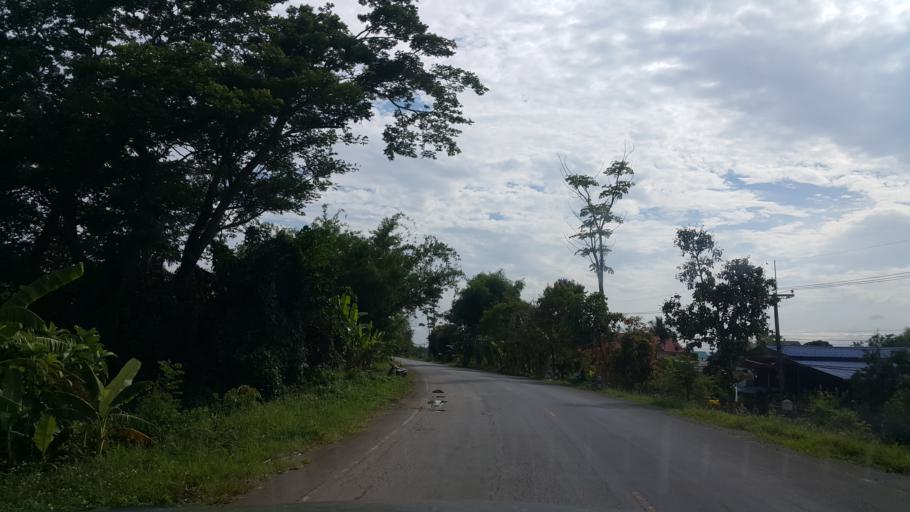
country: TH
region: Chiang Rai
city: Wiang Chai
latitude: 19.9532
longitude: 99.9323
